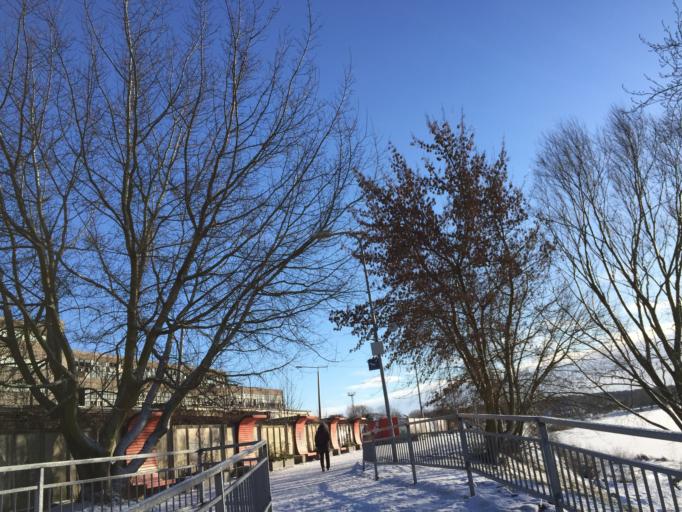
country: LV
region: Kekava
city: Balozi
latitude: 56.9039
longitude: 24.1868
